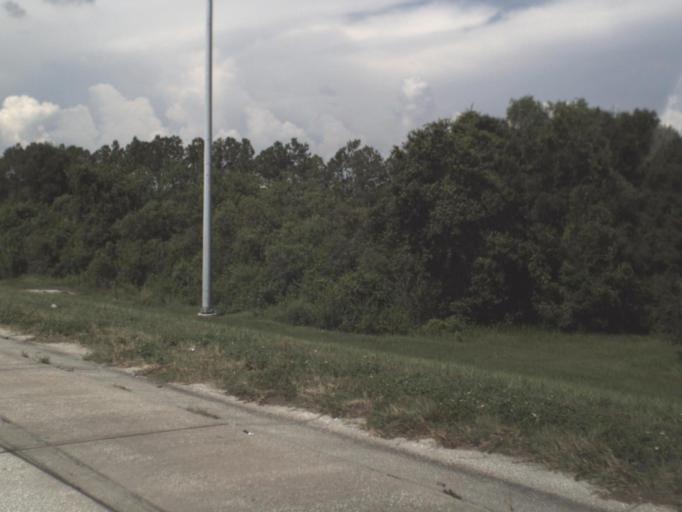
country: US
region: Florida
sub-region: Hillsborough County
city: Progress Village
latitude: 27.9008
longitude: -82.3454
